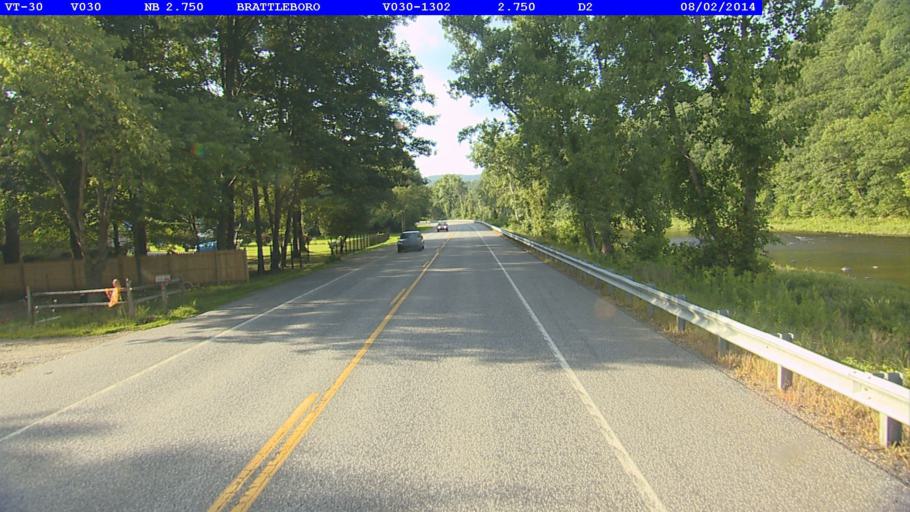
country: US
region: Vermont
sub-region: Windham County
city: West Brattleboro
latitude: 42.8884
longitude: -72.5896
